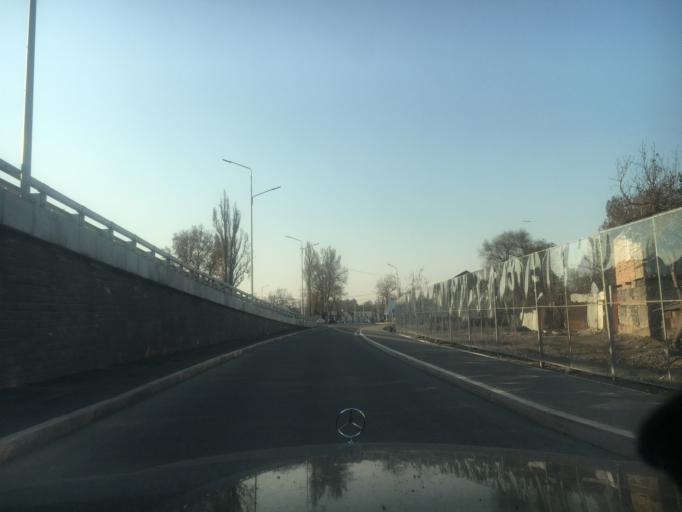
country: KZ
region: Almaty Qalasy
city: Almaty
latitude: 43.2781
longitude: 76.9415
